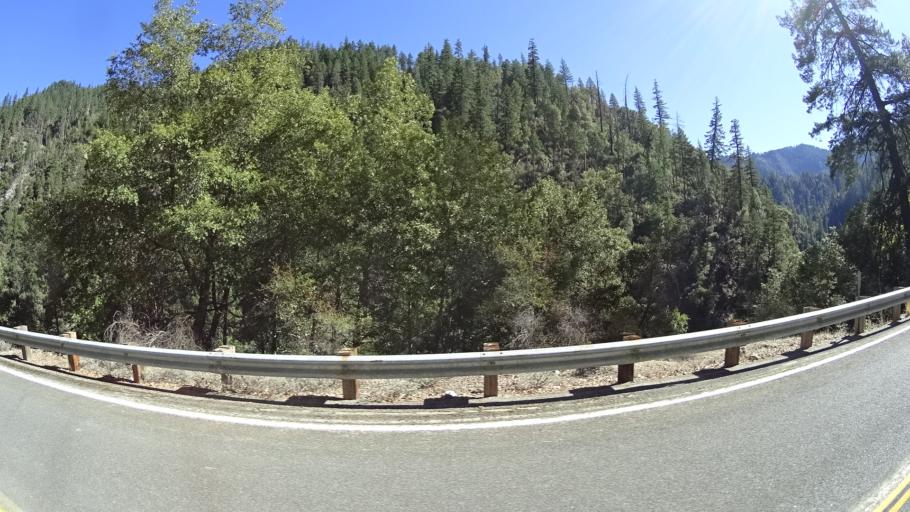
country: US
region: California
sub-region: Siskiyou County
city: Happy Camp
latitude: 41.3534
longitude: -123.4092
